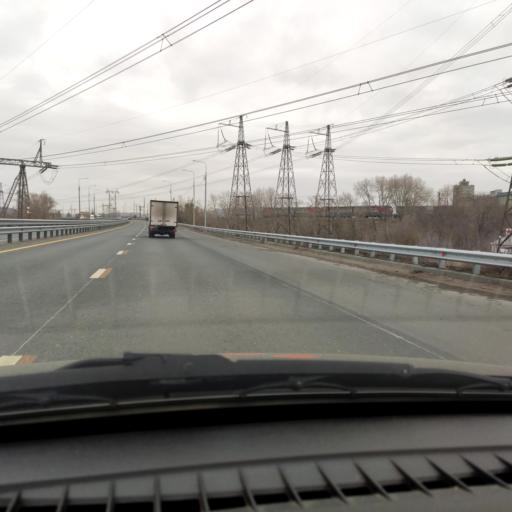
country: RU
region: Samara
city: Zhigulevsk
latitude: 53.4726
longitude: 49.5062
